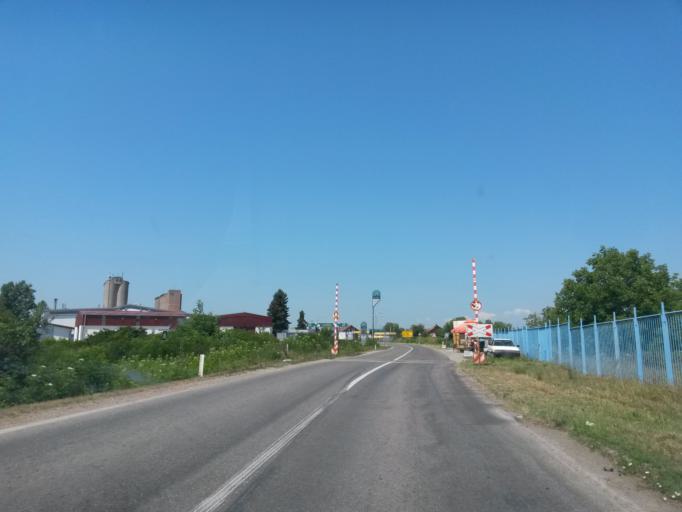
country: BA
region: Republika Srpska
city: Bosanski Samac
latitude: 45.0534
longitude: 18.4805
